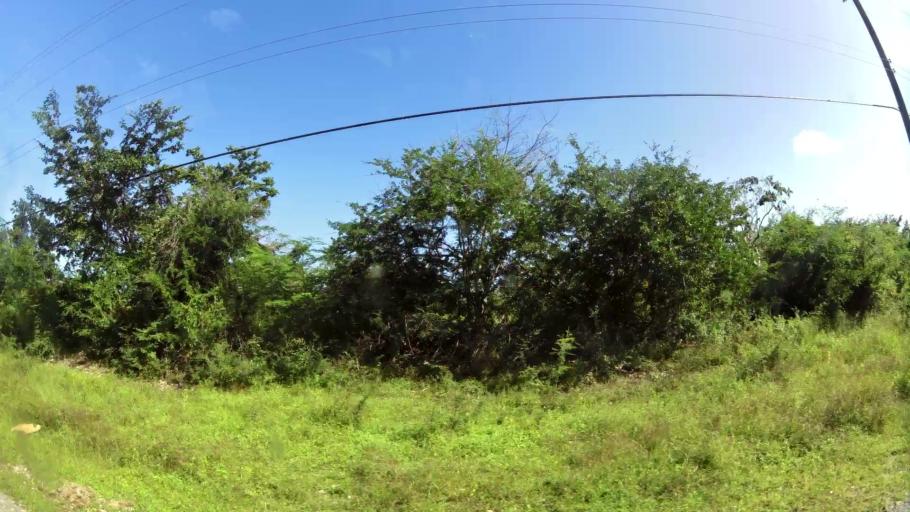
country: AG
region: Barbuda
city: Codrington
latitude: 17.6123
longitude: -61.8284
